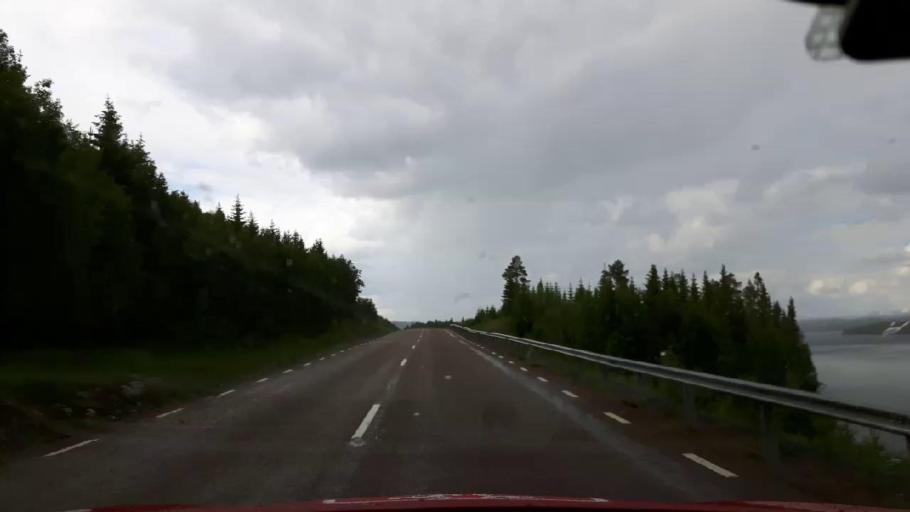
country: SE
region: Jaemtland
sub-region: Krokoms Kommun
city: Valla
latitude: 63.8868
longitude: 14.2791
